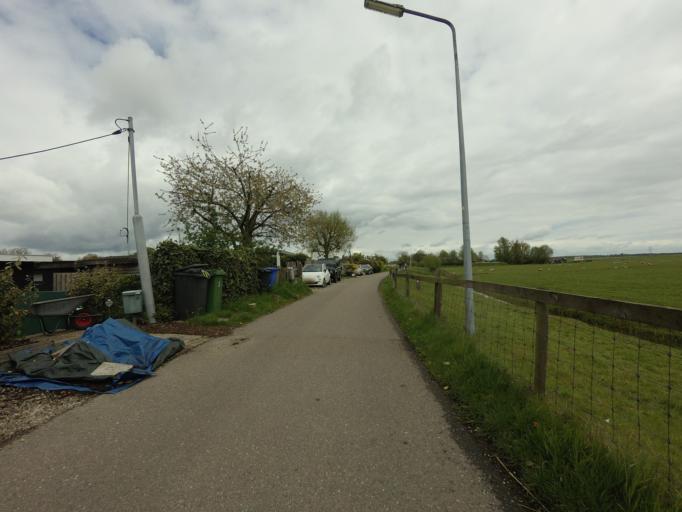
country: NL
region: North Holland
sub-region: Gemeente Weesp
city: Weesp
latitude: 52.3149
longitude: 5.0530
